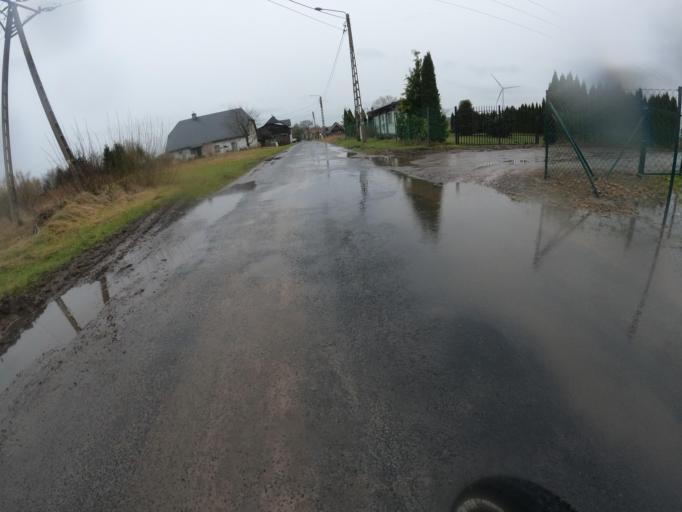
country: PL
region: West Pomeranian Voivodeship
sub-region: Powiat slawienski
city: Darlowo
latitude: 54.3991
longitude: 16.5328
